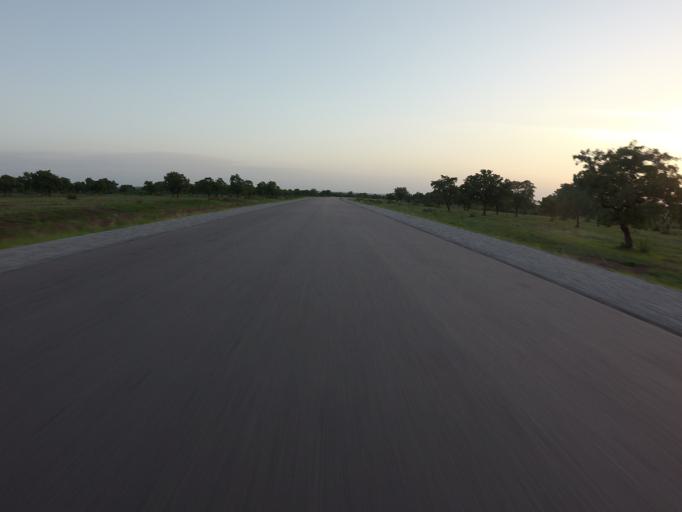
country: GH
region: Northern
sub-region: Yendi
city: Yendi
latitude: 9.9405
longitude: -0.1681
